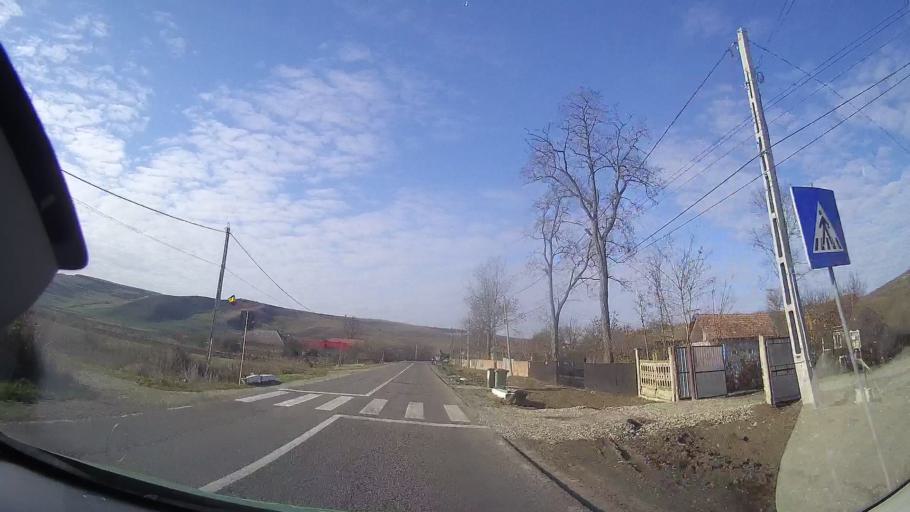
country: RO
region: Cluj
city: Caianu Mic
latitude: 46.7986
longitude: 23.8776
